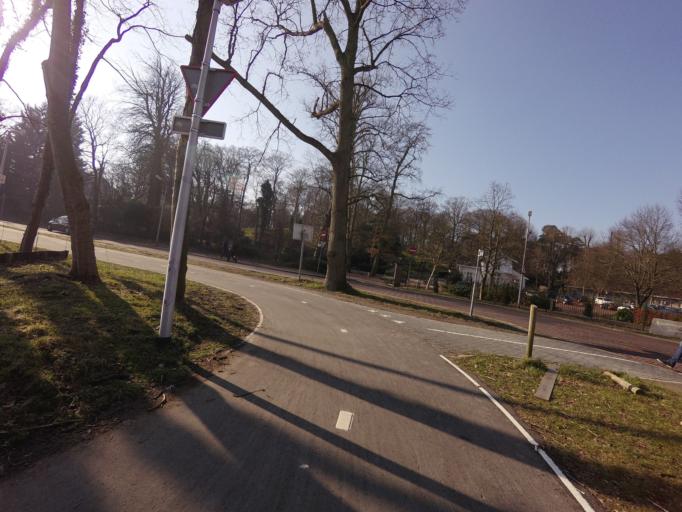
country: NL
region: North Holland
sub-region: Gemeente Velsen
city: Velsen-Zuid
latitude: 52.4443
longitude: 4.6325
